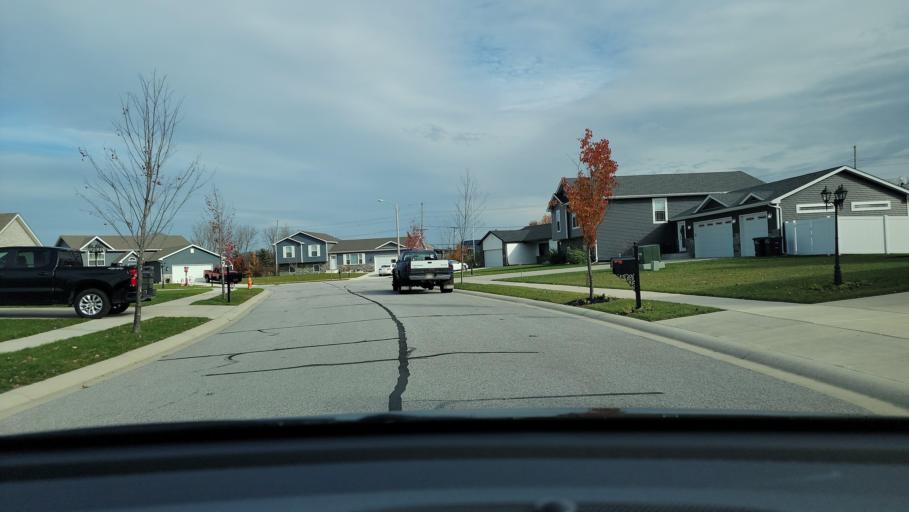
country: US
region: Indiana
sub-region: Porter County
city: South Haven
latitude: 41.5823
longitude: -87.1258
